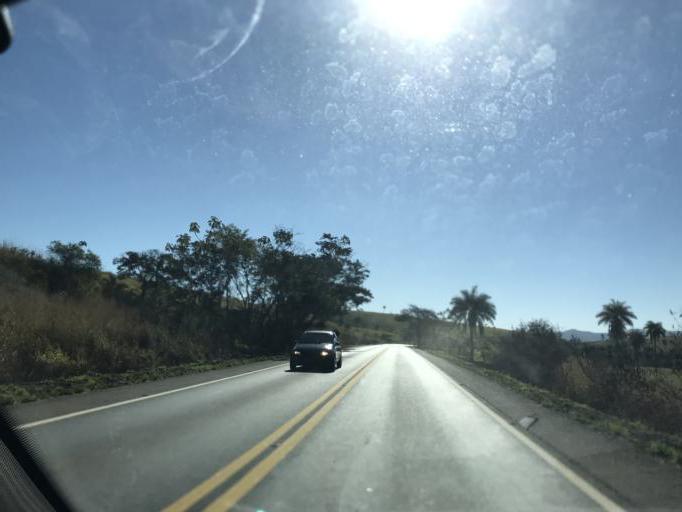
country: BR
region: Minas Gerais
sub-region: Bambui
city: Bambui
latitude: -19.8402
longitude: -46.0001
